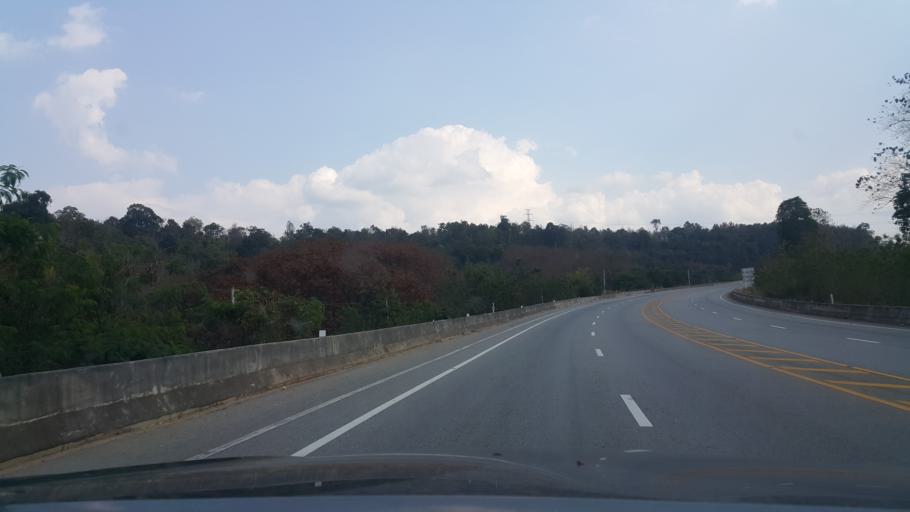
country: TH
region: Phitsanulok
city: Nakhon Thai
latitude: 16.8867
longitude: 100.8103
